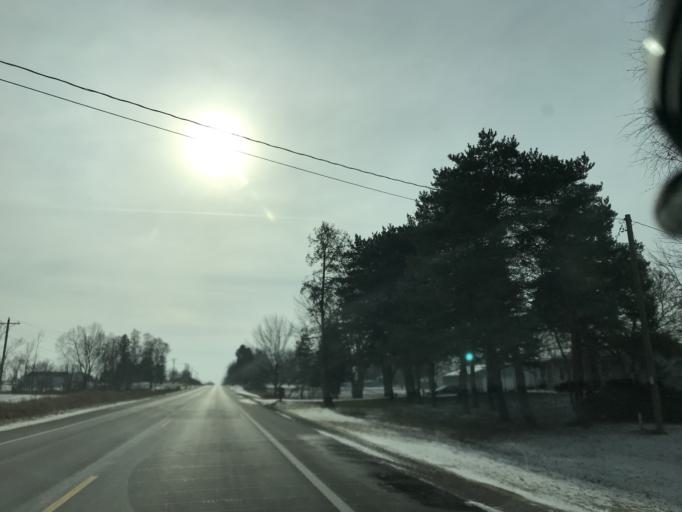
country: US
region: Michigan
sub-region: Ionia County
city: Lake Odessa
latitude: 42.7953
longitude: -85.0745
